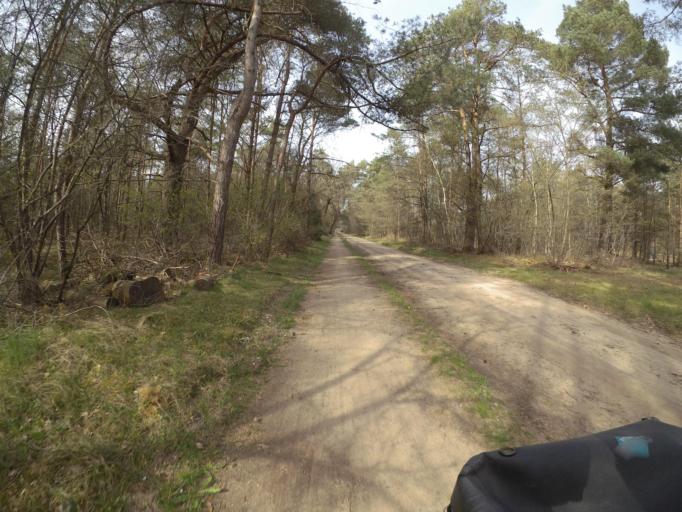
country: NL
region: Gelderland
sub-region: Gemeente Barneveld
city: Garderen
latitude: 52.2230
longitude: 5.7486
